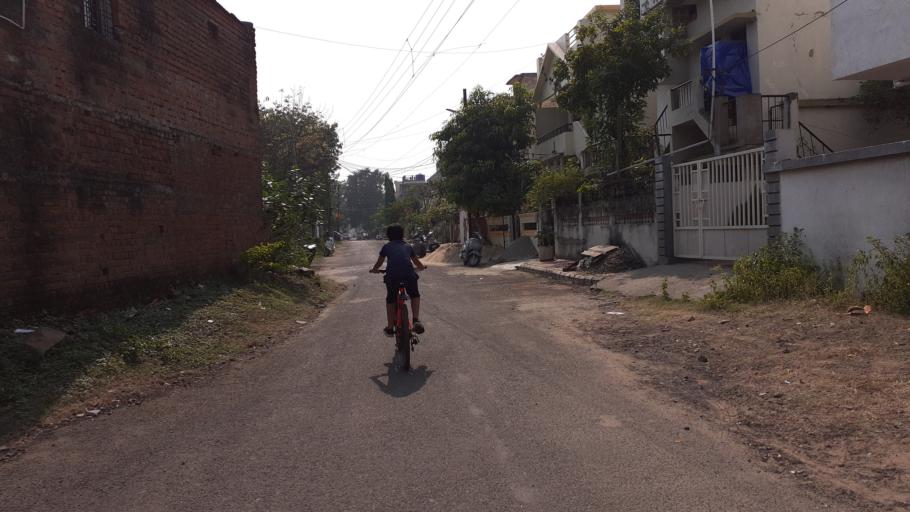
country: IN
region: Maharashtra
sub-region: Nagpur Division
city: Nagpur
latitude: 21.1127
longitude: 79.1170
